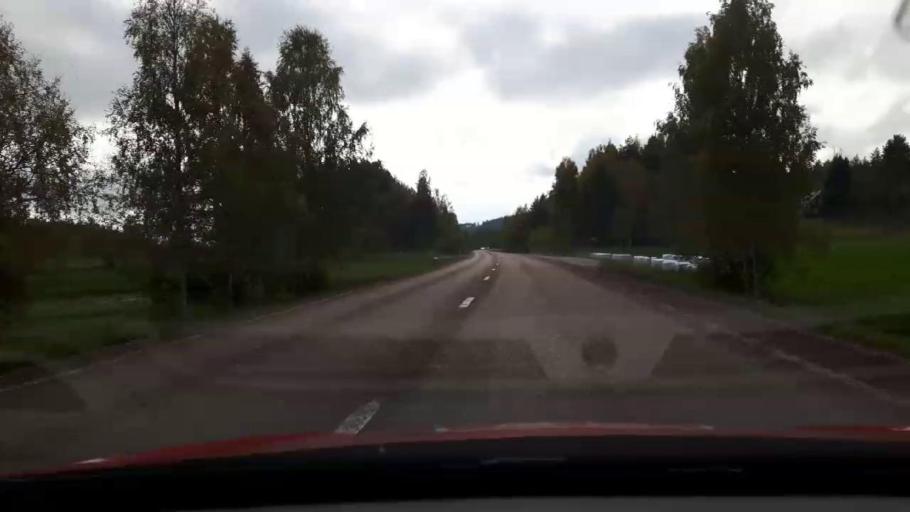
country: SE
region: Gaevleborg
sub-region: Bollnas Kommun
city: Arbra
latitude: 61.6085
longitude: 16.2953
